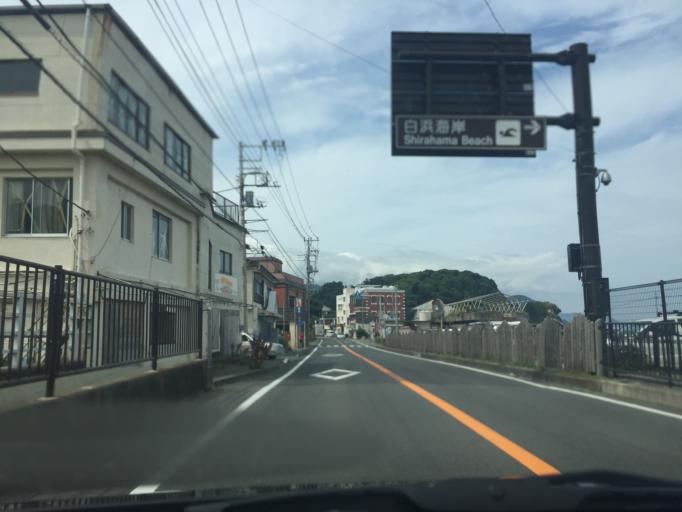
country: JP
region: Shizuoka
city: Shimoda
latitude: 34.6907
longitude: 138.9723
